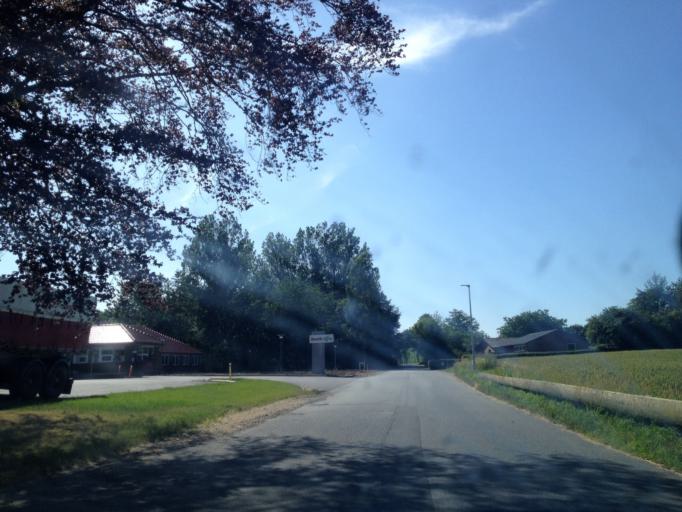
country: DK
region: South Denmark
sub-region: Kolding Kommune
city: Christiansfeld
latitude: 55.4005
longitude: 9.5242
